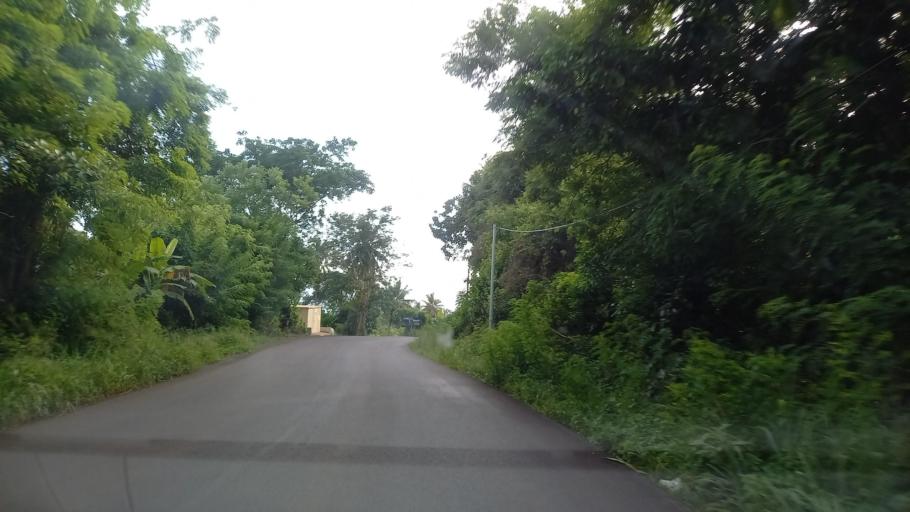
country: YT
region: M'Tsangamouji
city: M'Tsangamouji
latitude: -12.7486
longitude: 45.0616
